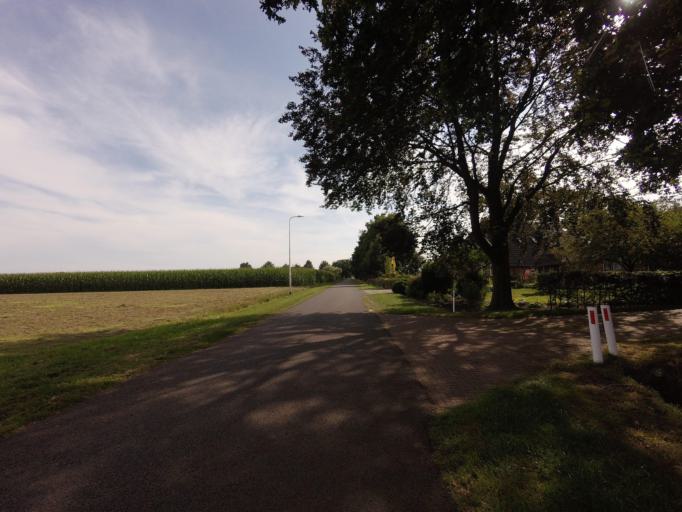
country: NL
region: Drenthe
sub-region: Gemeente Coevorden
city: Dalen
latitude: 52.7013
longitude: 6.7314
